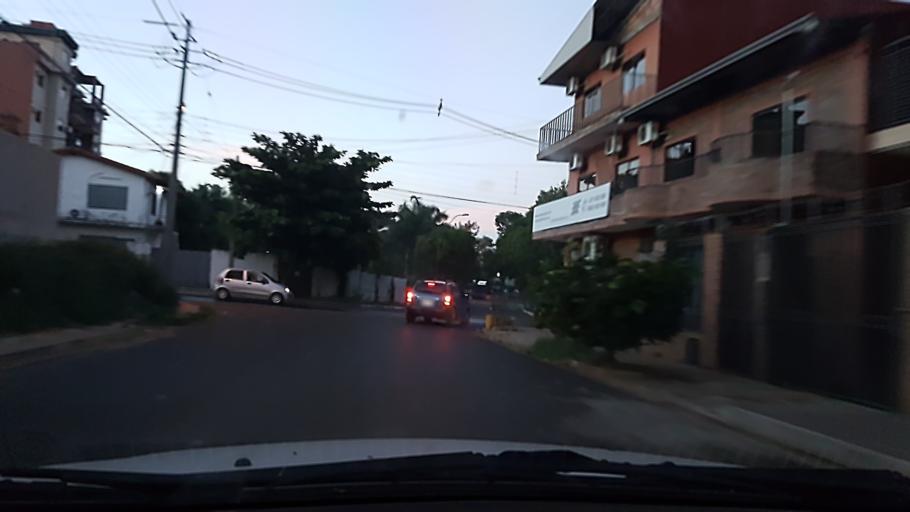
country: PY
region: Central
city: Fernando de la Mora
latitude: -25.3075
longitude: -57.5552
